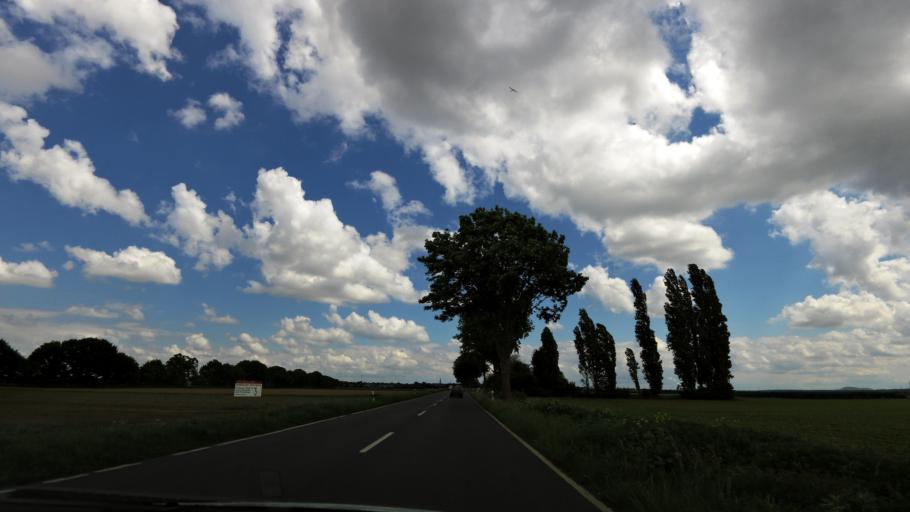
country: NL
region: Limburg
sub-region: Gemeente Onderbanken
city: Schinveld
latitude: 50.9940
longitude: 5.9709
